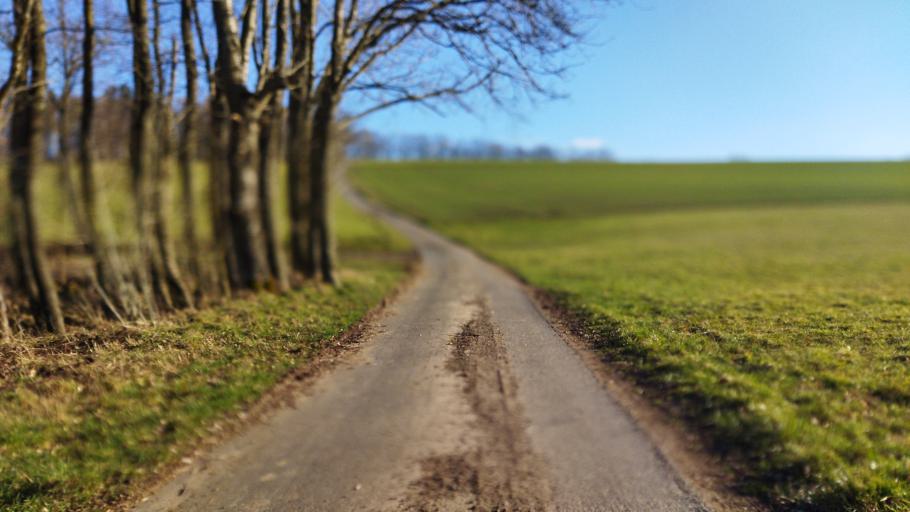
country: DE
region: Rheinland-Pfalz
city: Herchweiler
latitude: 49.4999
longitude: 7.2791
